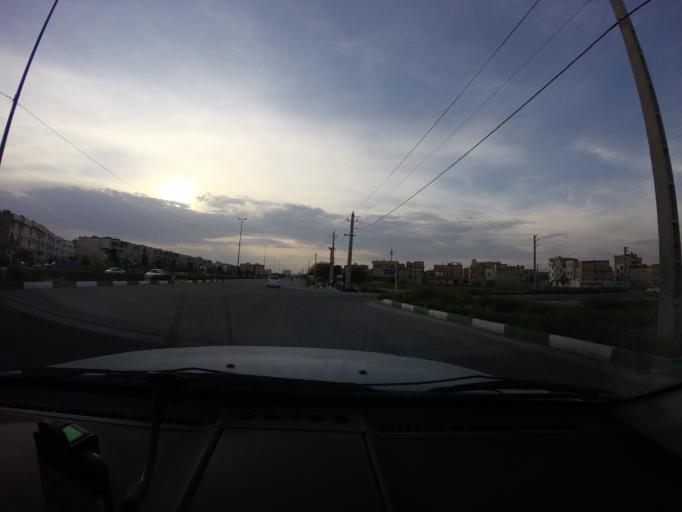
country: IR
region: Tehran
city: Eslamshahr
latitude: 35.5346
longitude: 51.2316
